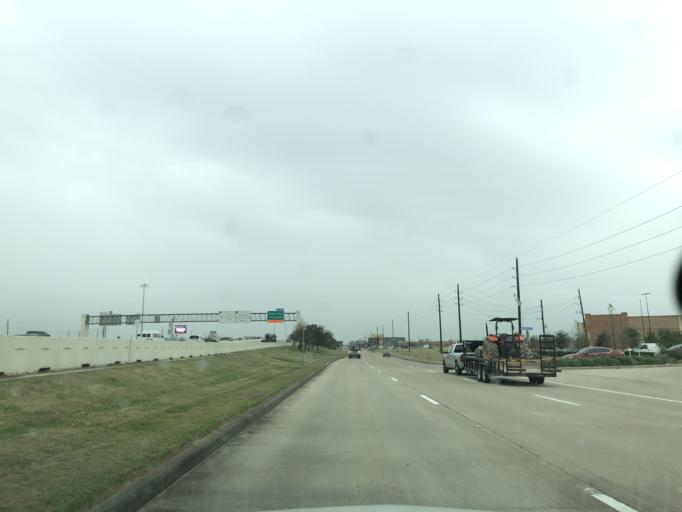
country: US
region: Texas
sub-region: Fort Bend County
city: Sugar Land
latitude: 29.5840
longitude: -95.6441
